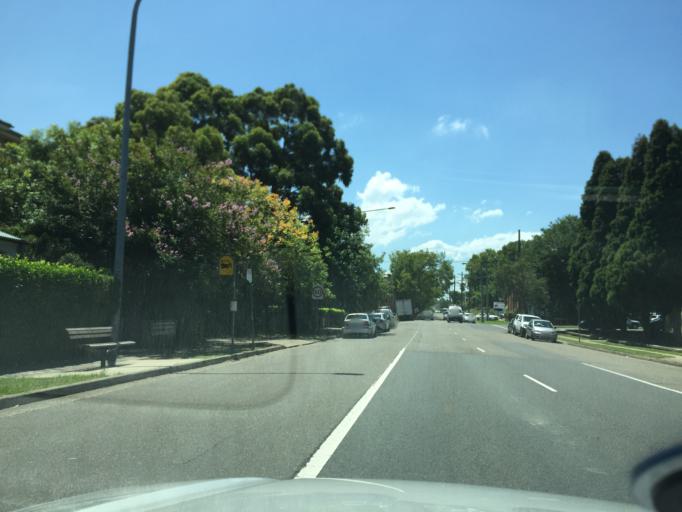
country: AU
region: New South Wales
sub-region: Parramatta
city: City of Parramatta
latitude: -33.8001
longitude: 151.0024
